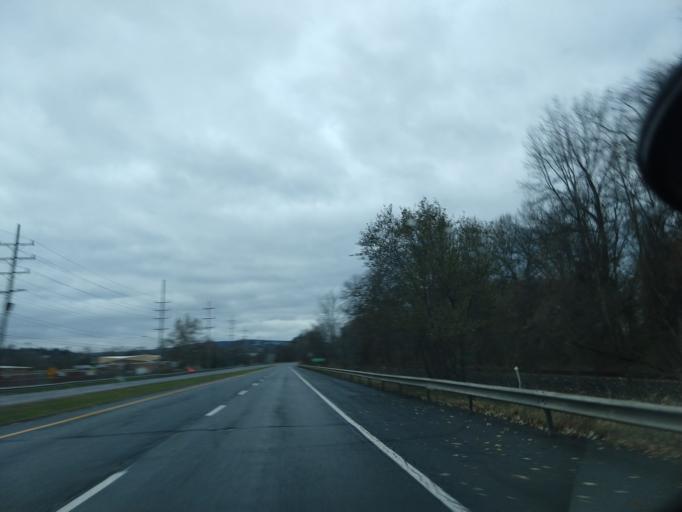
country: US
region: New York
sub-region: Tompkins County
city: Cayuga Heights
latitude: 42.4584
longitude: -76.5006
